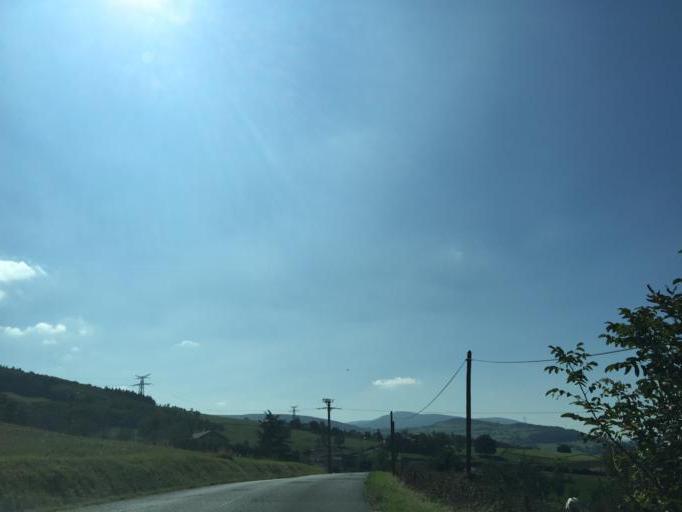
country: FR
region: Rhone-Alpes
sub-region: Departement de la Loire
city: Saint-Paul-en-Jarez
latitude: 45.4762
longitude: 4.5672
